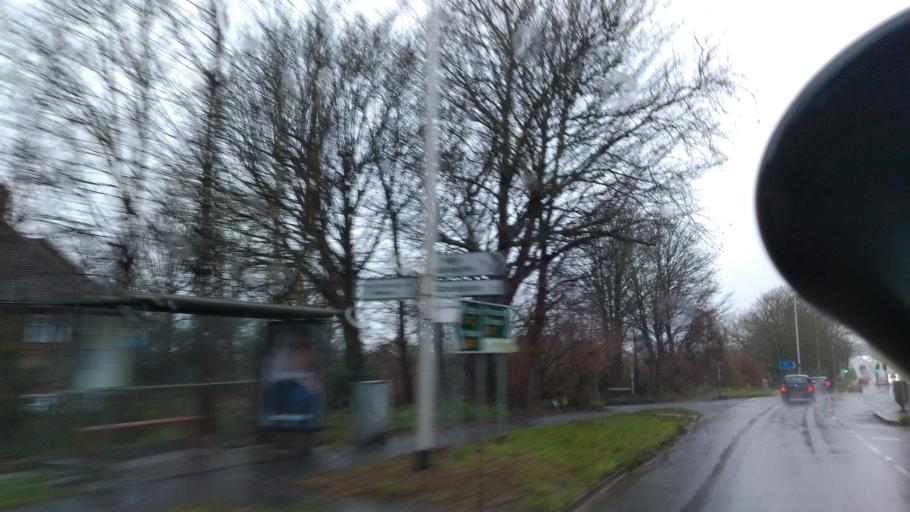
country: GB
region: England
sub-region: West Sussex
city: Findon
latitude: 50.8407
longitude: -0.4102
